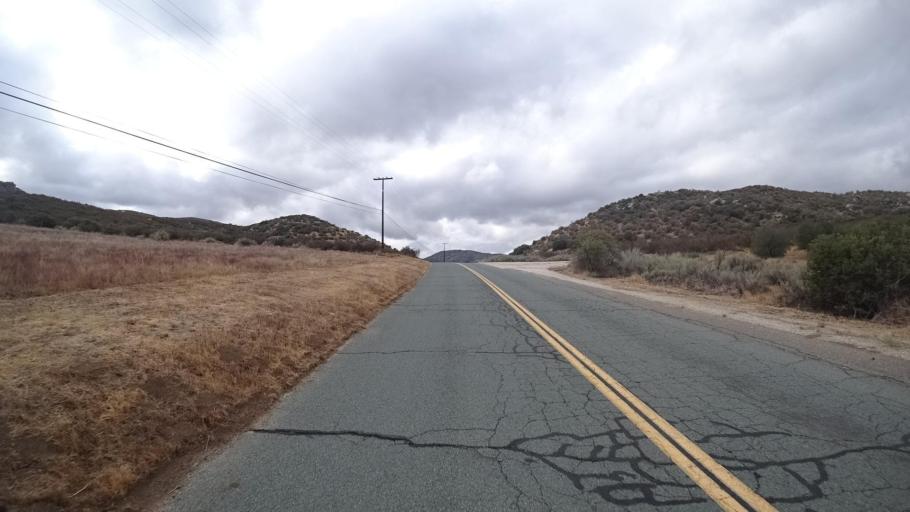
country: US
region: California
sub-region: San Diego County
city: Campo
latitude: 32.7079
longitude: -116.4314
